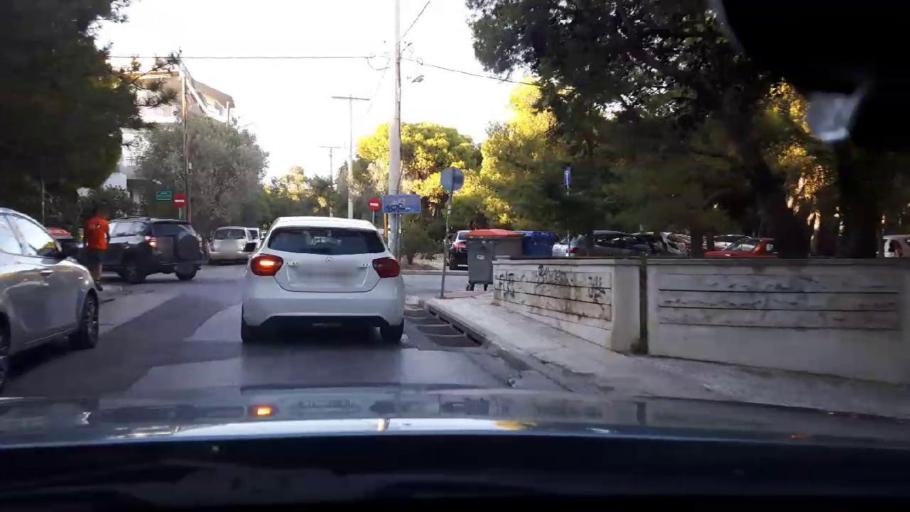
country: GR
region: Attica
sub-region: Nomarchia Athinas
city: Melissia
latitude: 38.0492
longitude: 23.8338
